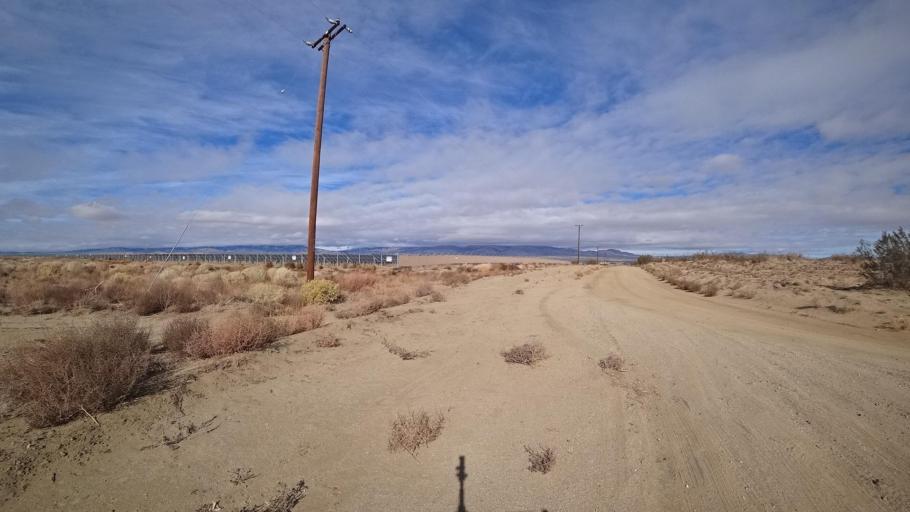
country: US
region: California
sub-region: Kern County
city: Rosamond
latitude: 34.8340
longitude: -118.3616
